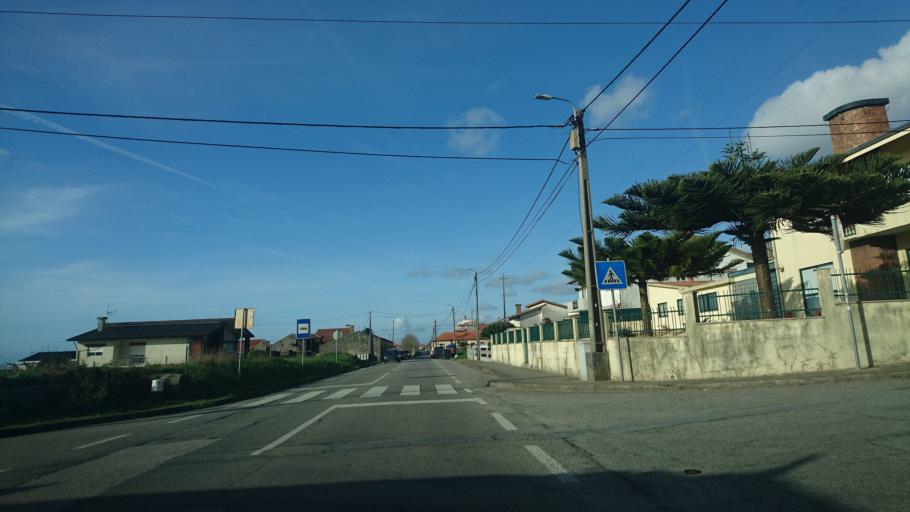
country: PT
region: Aveiro
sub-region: Ovar
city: Esmoriz
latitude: 40.9643
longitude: -8.6288
